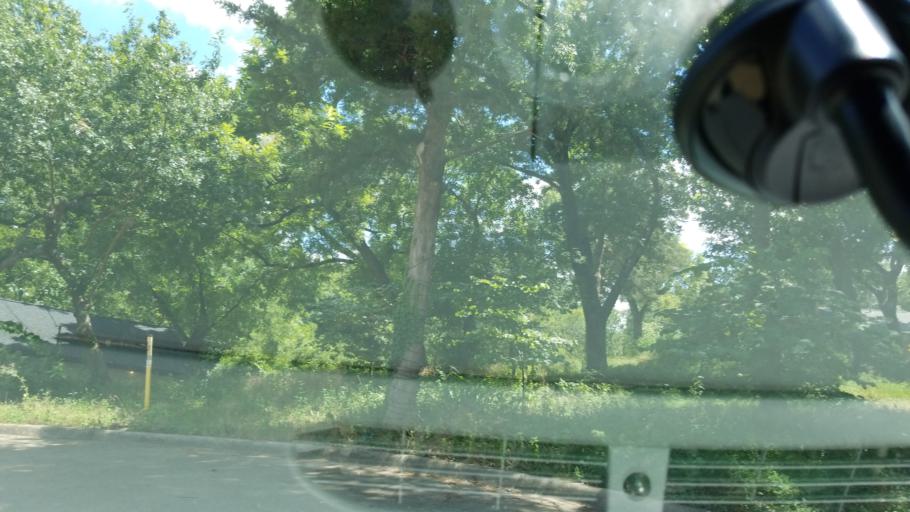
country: US
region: Texas
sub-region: Dallas County
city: Cockrell Hill
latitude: 32.7039
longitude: -96.8688
